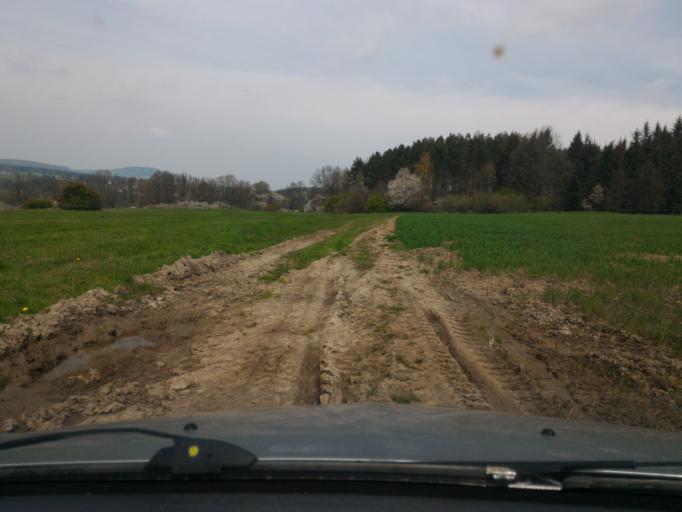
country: DE
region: Saxony
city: Hainewalde
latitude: 50.9108
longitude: 14.7214
